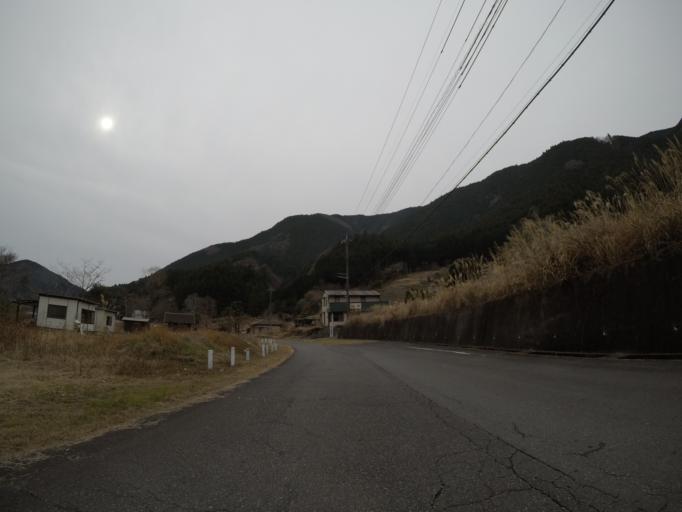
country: JP
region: Shizuoka
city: Fujinomiya
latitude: 35.2639
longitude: 138.5303
